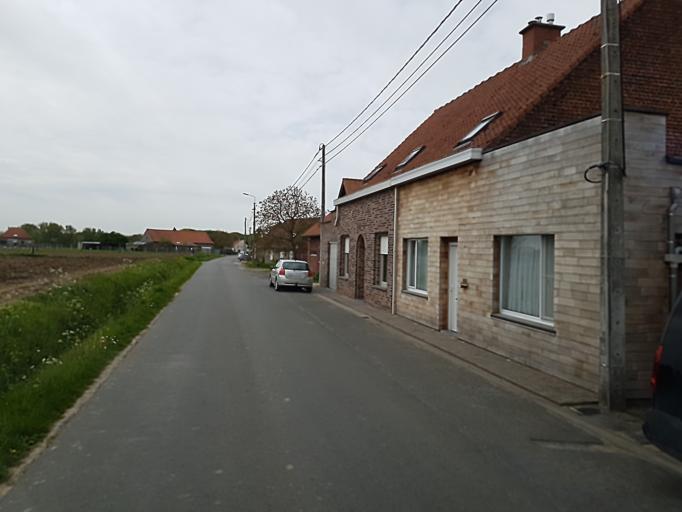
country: BE
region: Flanders
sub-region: Provincie West-Vlaanderen
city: Zonnebeke
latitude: 50.8525
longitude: 3.0054
